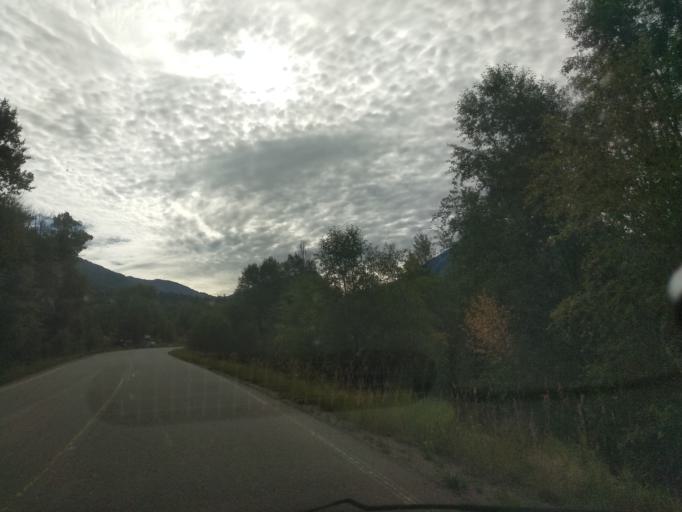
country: US
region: Colorado
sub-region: Gunnison County
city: Crested Butte
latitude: 39.0738
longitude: -107.2065
